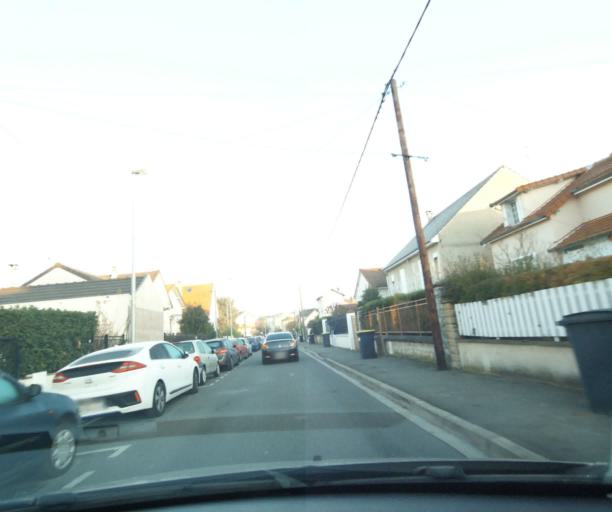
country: FR
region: Ile-de-France
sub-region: Departement de Seine-Saint-Denis
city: Gagny
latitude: 48.8791
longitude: 2.5250
